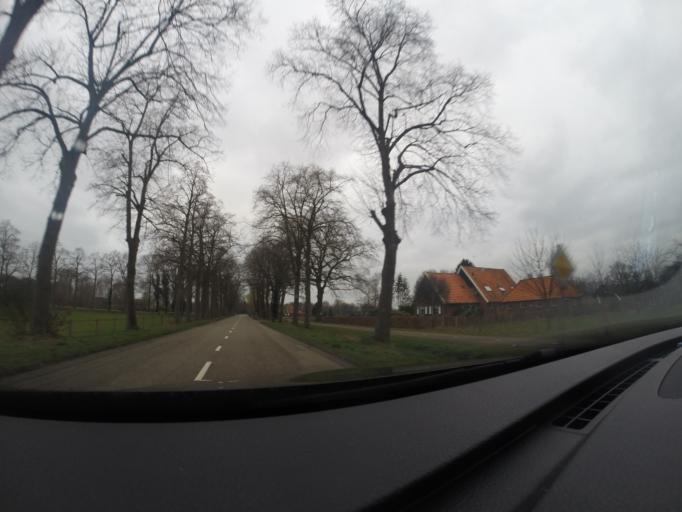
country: NL
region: Gelderland
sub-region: Berkelland
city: Eibergen
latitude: 52.0911
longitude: 6.7071
